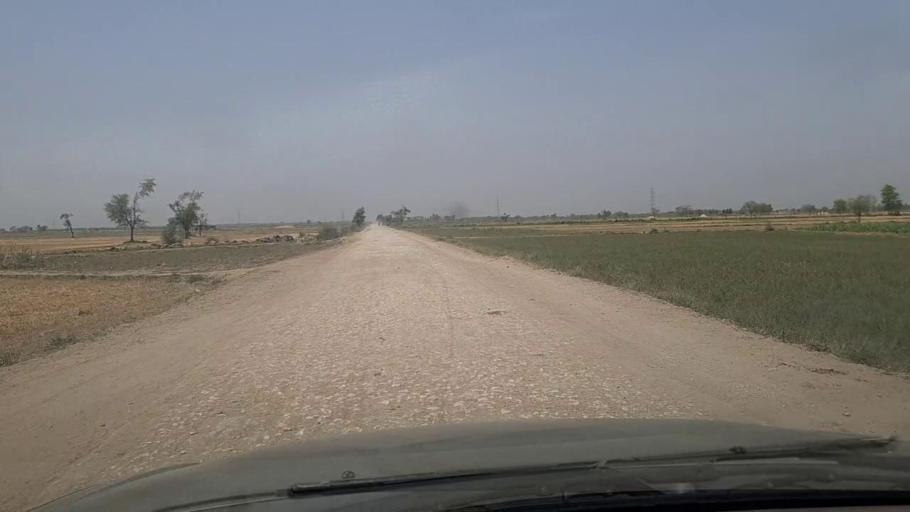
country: PK
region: Sindh
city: Adilpur
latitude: 27.9401
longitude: 69.3088
